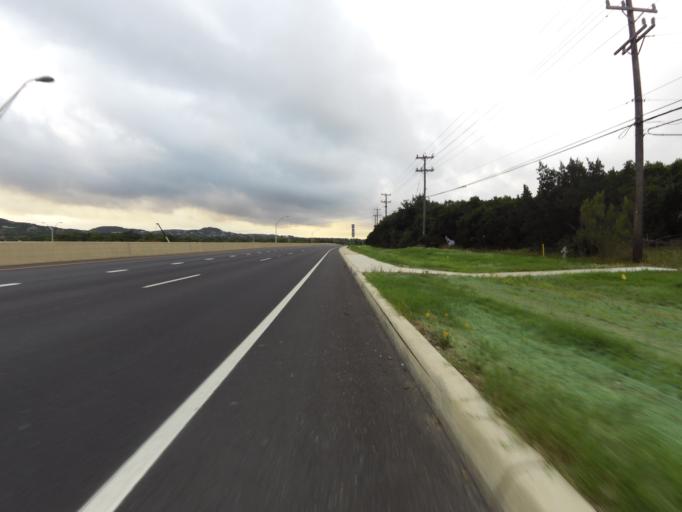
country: US
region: Texas
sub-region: Bexar County
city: Cross Mountain
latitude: 29.6604
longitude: -98.6286
